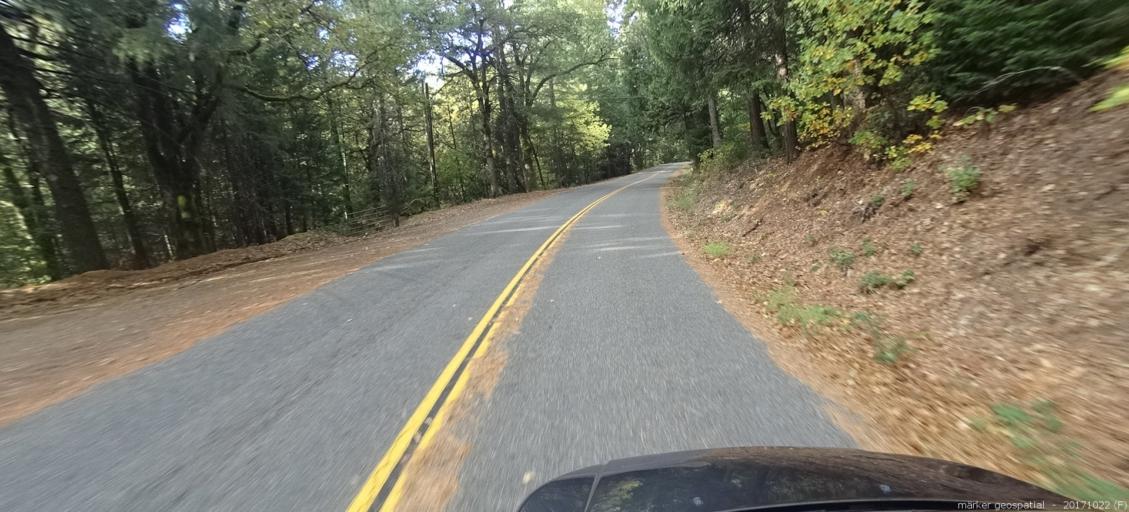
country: US
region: California
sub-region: Siskiyou County
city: Dunsmuir
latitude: 41.1512
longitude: -122.3001
